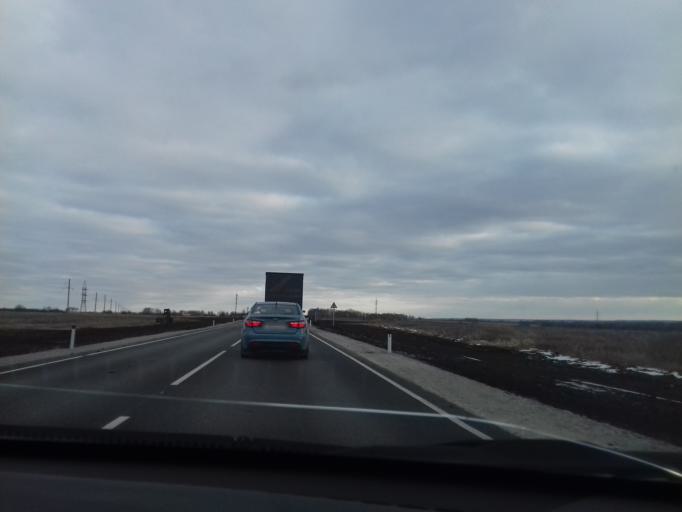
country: RU
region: Kurgan
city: Kataysk
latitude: 56.2943
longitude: 62.6691
